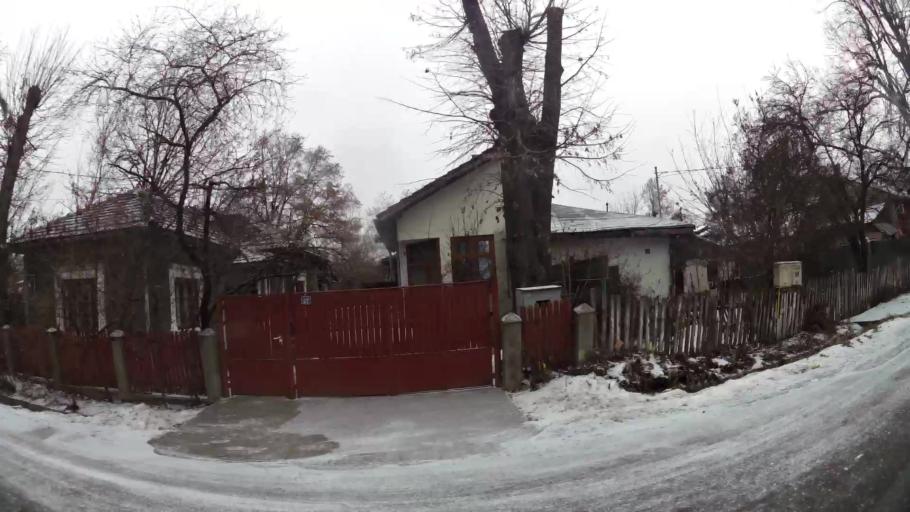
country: RO
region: Dambovita
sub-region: Municipiul Targoviste
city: Targoviste
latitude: 44.9386
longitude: 25.4743
